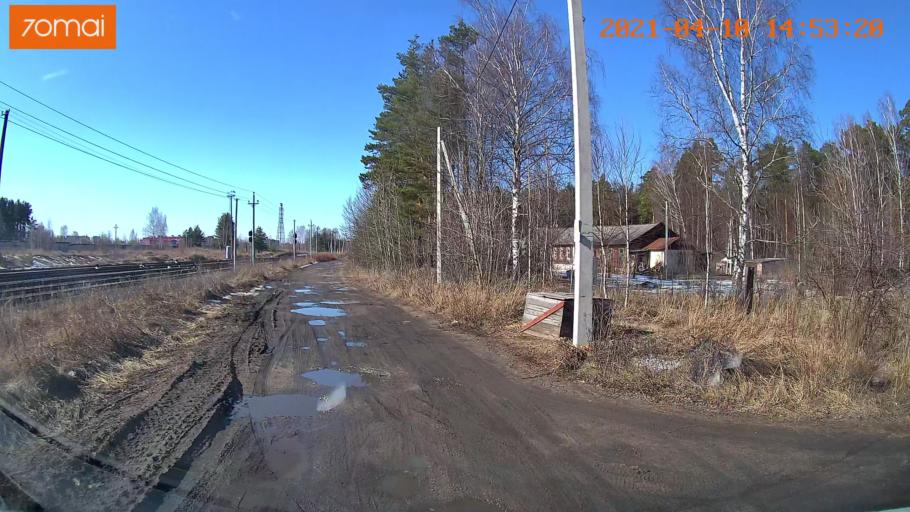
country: RU
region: Ivanovo
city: Kokhma
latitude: 56.9861
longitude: 41.0606
